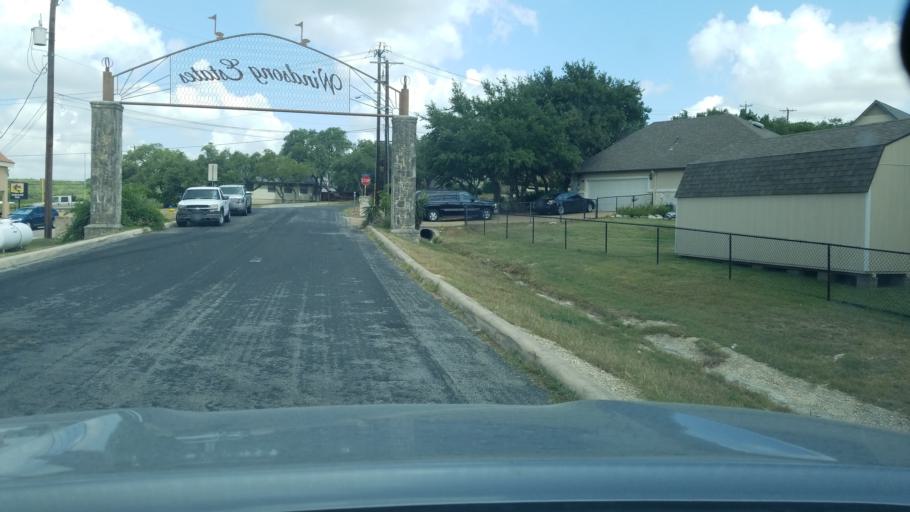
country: US
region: Texas
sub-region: Bexar County
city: Timberwood Park
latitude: 29.6745
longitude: -98.5215
